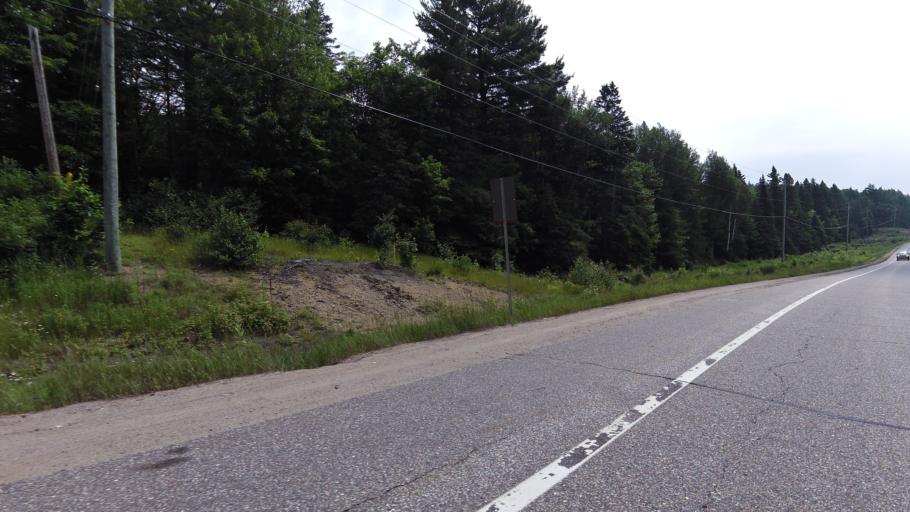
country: CA
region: Ontario
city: Mattawa
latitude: 45.5865
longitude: -78.4798
